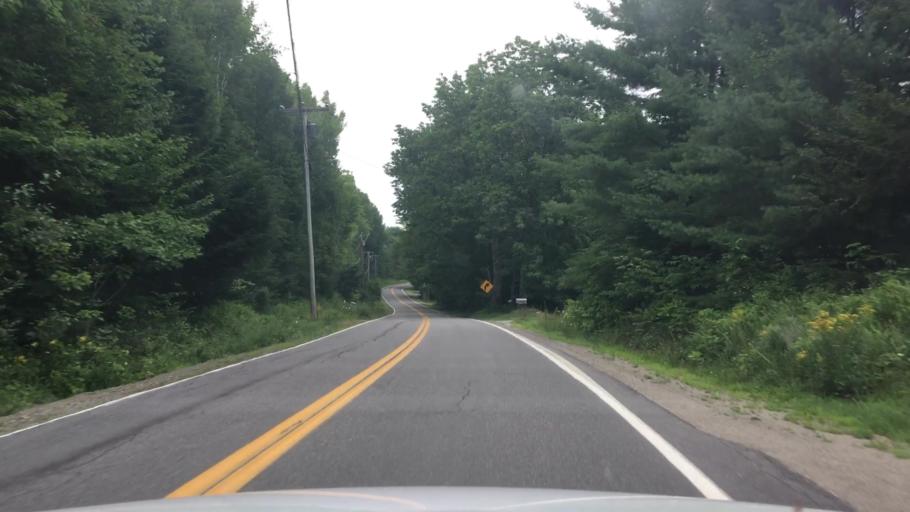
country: US
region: Maine
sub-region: Knox County
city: Washington
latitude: 44.2467
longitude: -69.3820
